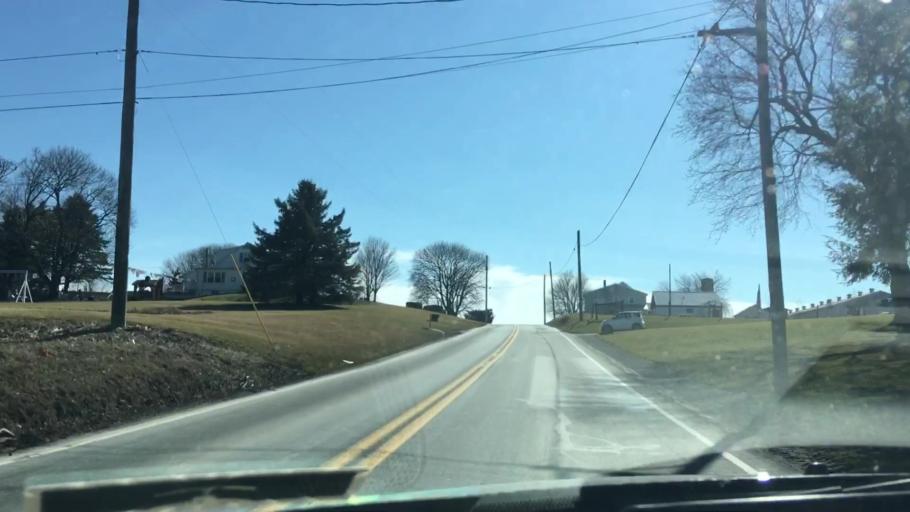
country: US
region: Pennsylvania
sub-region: Lancaster County
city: New Holland
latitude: 40.1024
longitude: -76.1393
